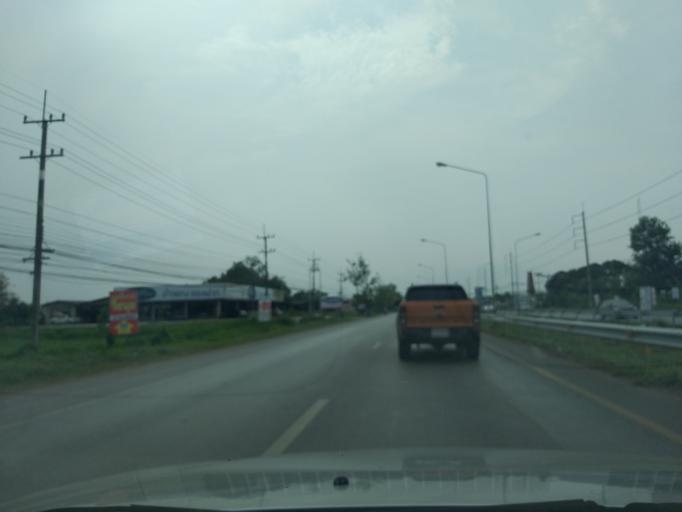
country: TH
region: Rayong
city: Klaeng
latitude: 12.7791
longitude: 101.7027
